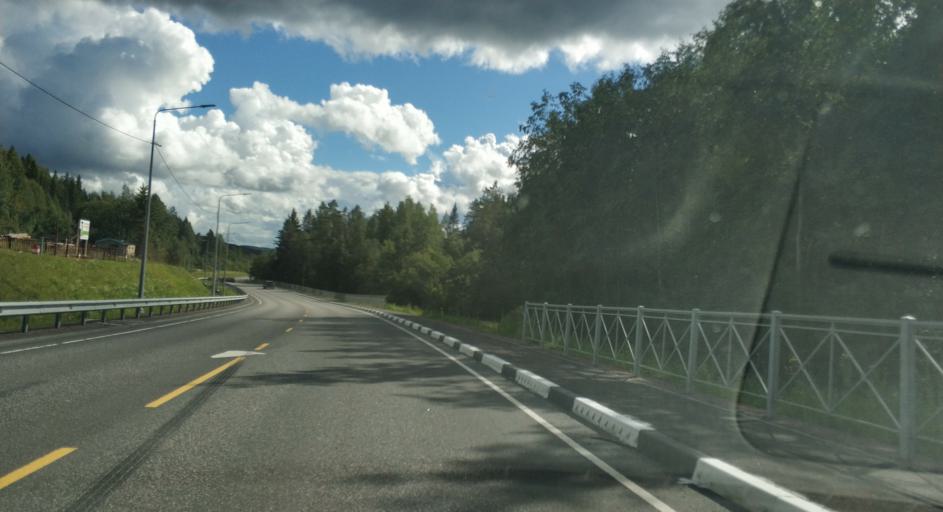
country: RU
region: Republic of Karelia
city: Ruskeala
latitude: 61.9264
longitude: 30.6005
